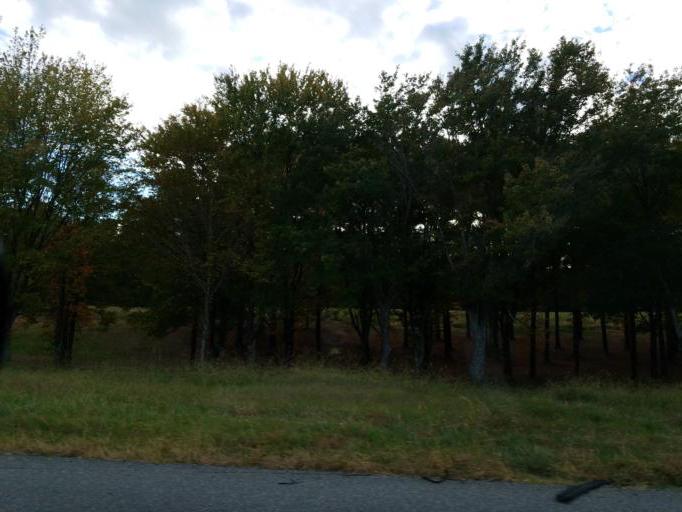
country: US
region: Georgia
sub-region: Bartow County
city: Emerson
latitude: 34.1415
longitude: -84.7385
